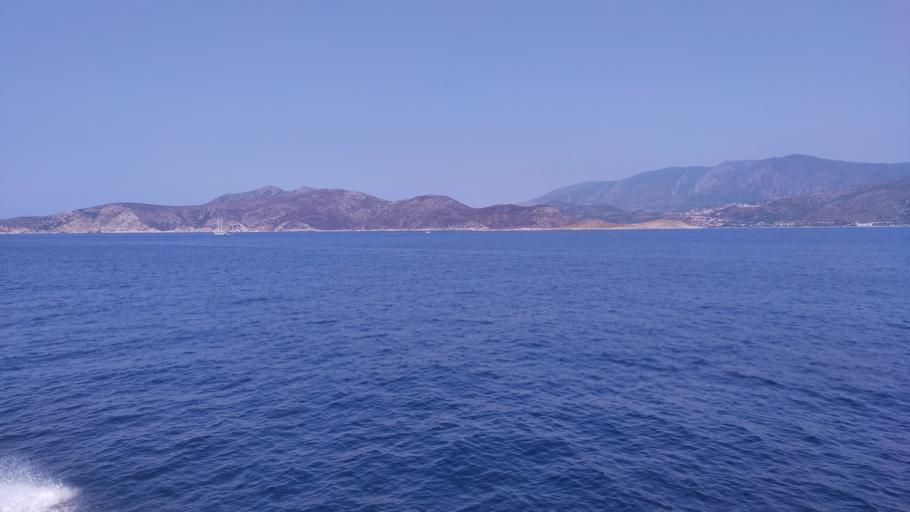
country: TR
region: Mugla
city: Datca
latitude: 36.6430
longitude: 27.5241
